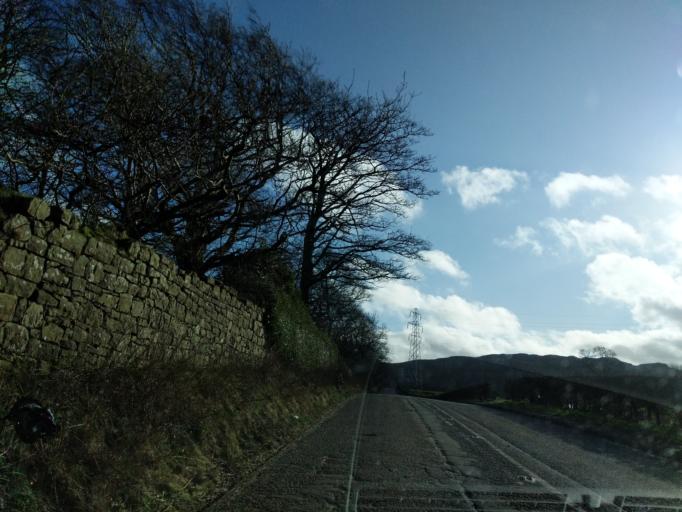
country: GB
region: Scotland
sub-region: Edinburgh
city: Ratho
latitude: 55.8983
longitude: -3.3855
